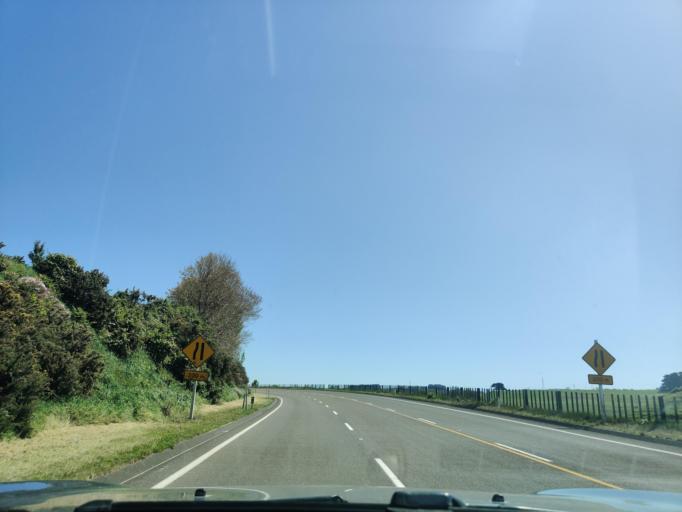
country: NZ
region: Manawatu-Wanganui
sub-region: Wanganui District
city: Wanganui
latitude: -39.8235
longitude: 174.8728
